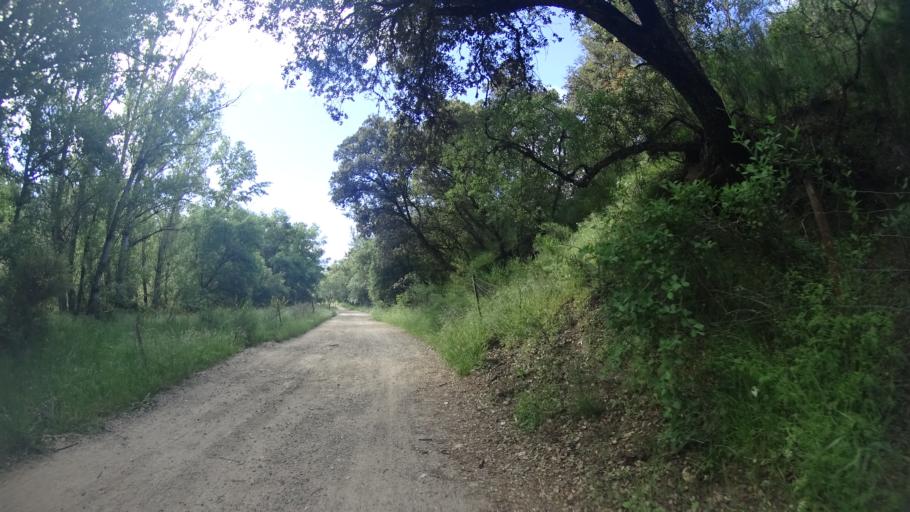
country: ES
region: Madrid
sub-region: Provincia de Madrid
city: Brunete
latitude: 40.4254
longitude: -3.9524
